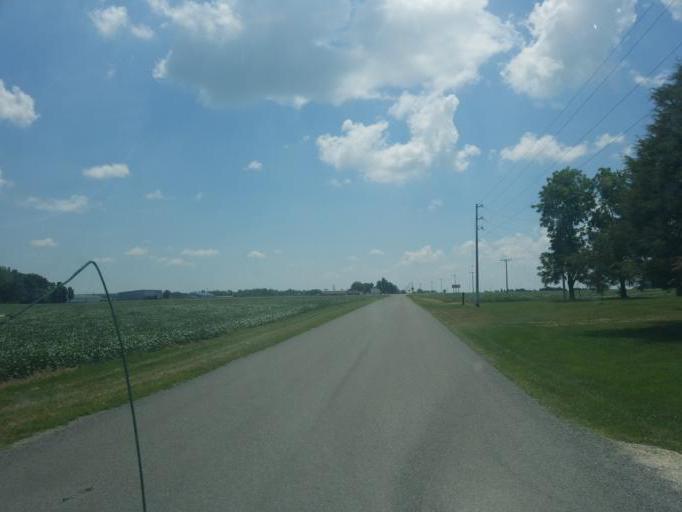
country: US
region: Ohio
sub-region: Mercer County
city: Celina
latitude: 40.5604
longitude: -84.4939
